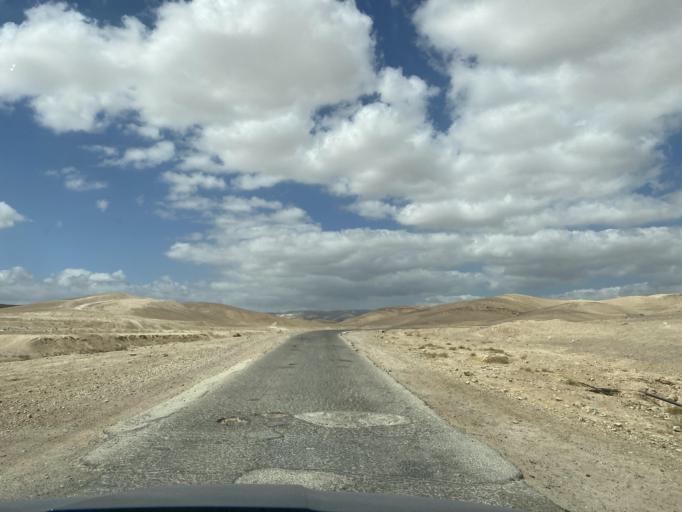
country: PS
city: `Arab ar Rashaydah
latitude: 31.5326
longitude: 35.2793
